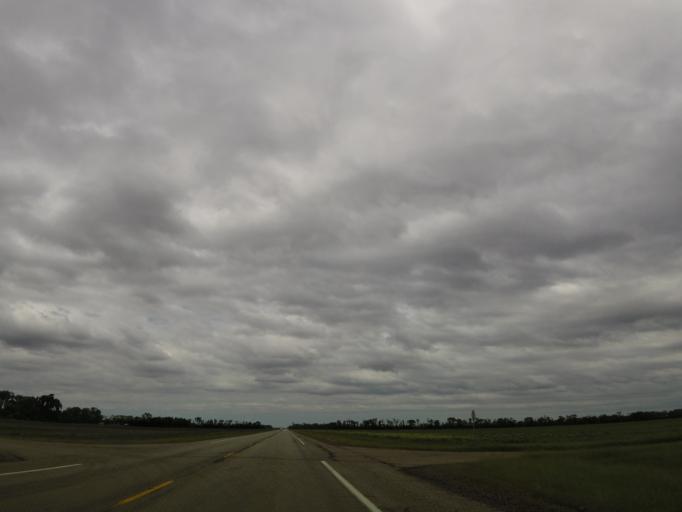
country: US
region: North Dakota
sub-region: Walsh County
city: Grafton
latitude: 48.5280
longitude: -97.4476
